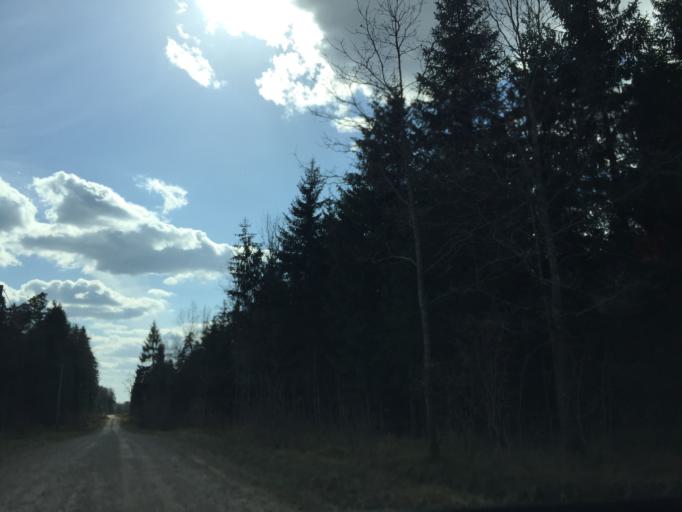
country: LV
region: Aizkraukles Rajons
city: Aizkraukle
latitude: 56.7902
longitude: 25.2427
